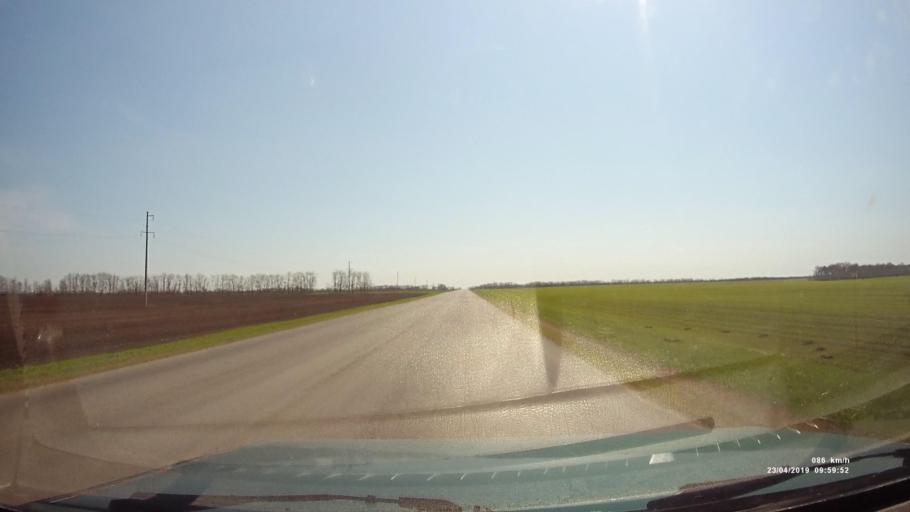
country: RU
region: Rostov
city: Sovetskoye
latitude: 46.7732
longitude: 42.1211
